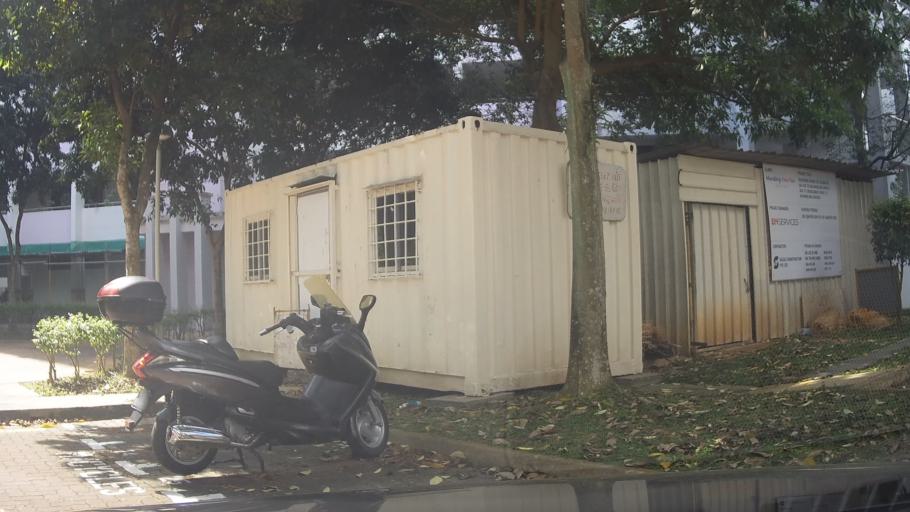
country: MY
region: Johor
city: Johor Bahru
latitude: 1.4436
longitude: 103.7754
